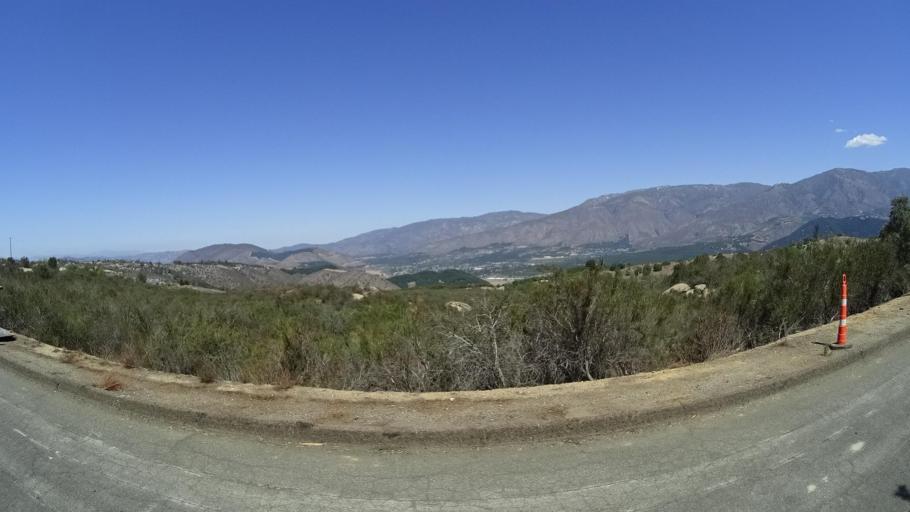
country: US
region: California
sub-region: San Diego County
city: Valley Center
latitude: 33.2821
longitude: -117.0042
